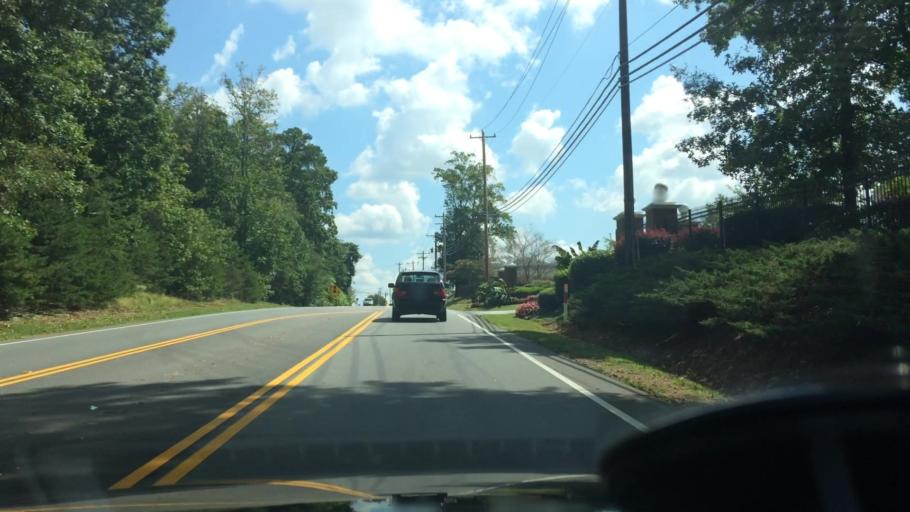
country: US
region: South Carolina
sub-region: Greenville County
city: Berea
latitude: 34.9138
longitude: -82.4327
